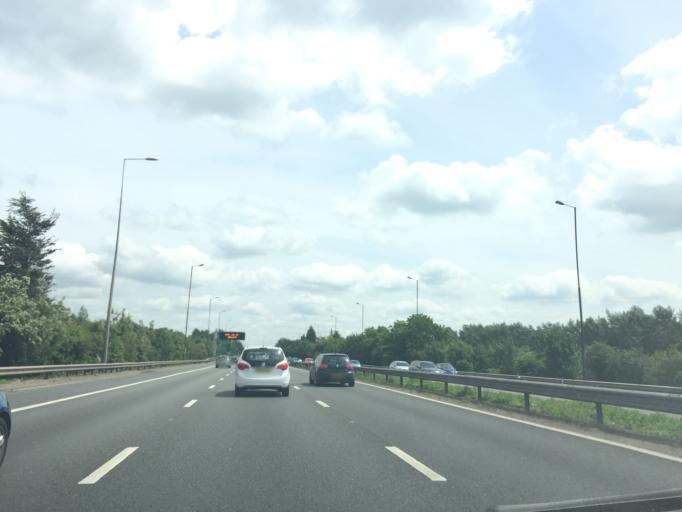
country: GB
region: England
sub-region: Kent
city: Dartford
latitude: 51.4307
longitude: 0.2033
